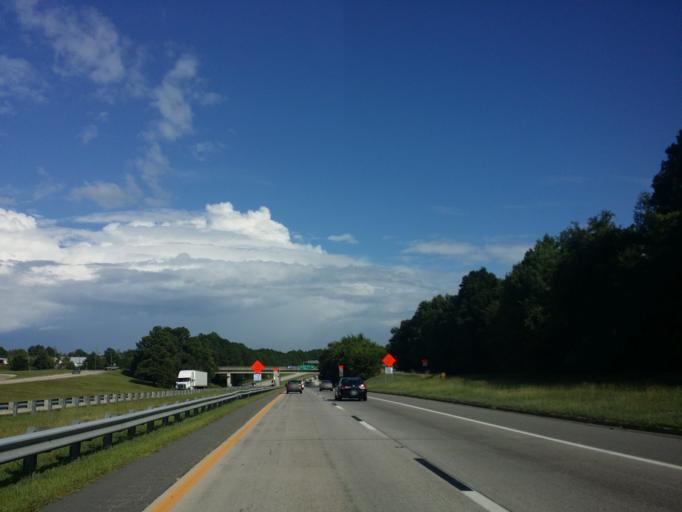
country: US
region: North Carolina
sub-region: Durham County
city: Durham
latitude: 35.9774
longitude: -78.8786
